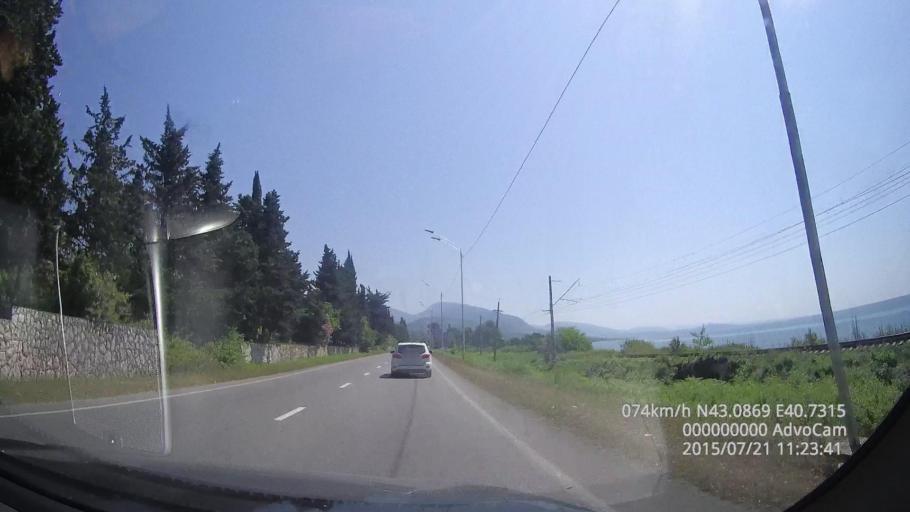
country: GE
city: P'rimorsk'oe
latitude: 43.0870
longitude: 40.7321
